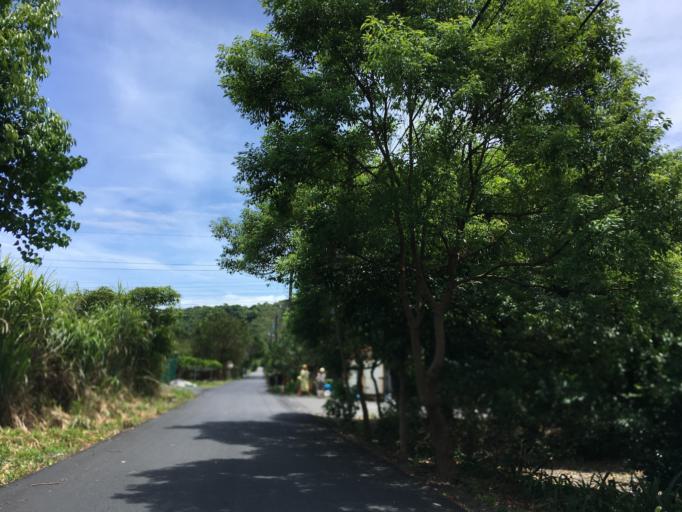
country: TW
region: Taiwan
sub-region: Yilan
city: Yilan
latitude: 24.6348
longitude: 121.7182
